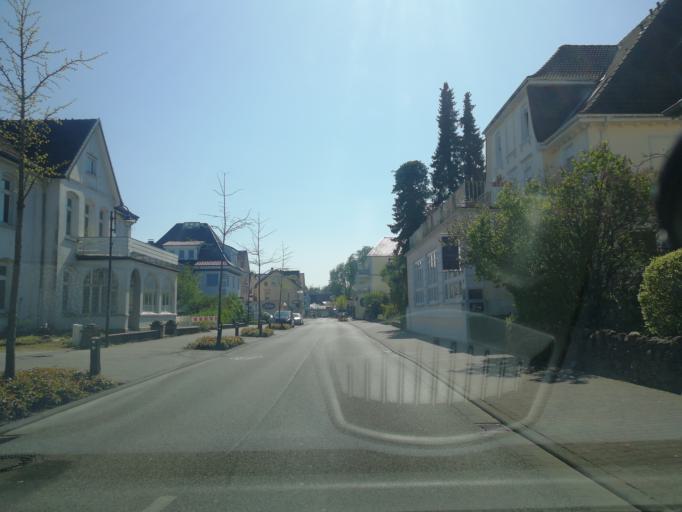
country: DE
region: Lower Saxony
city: Bad Rothenfelde
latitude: 52.1127
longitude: 8.1621
